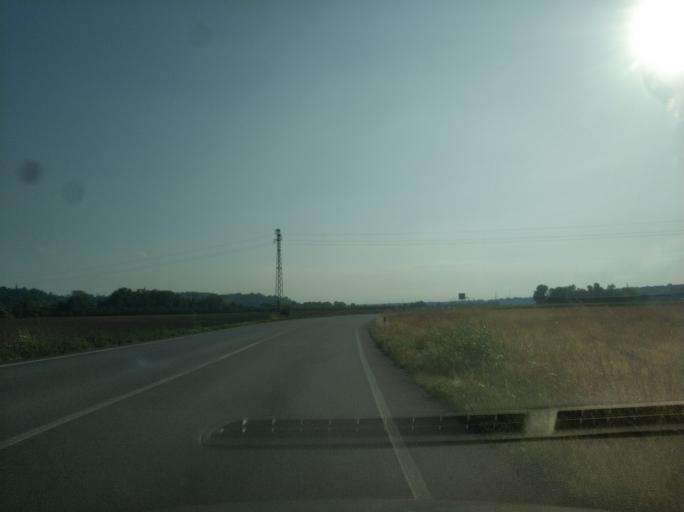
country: IT
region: Piedmont
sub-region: Provincia di Cuneo
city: Cherasco
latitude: 44.6686
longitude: 7.8600
